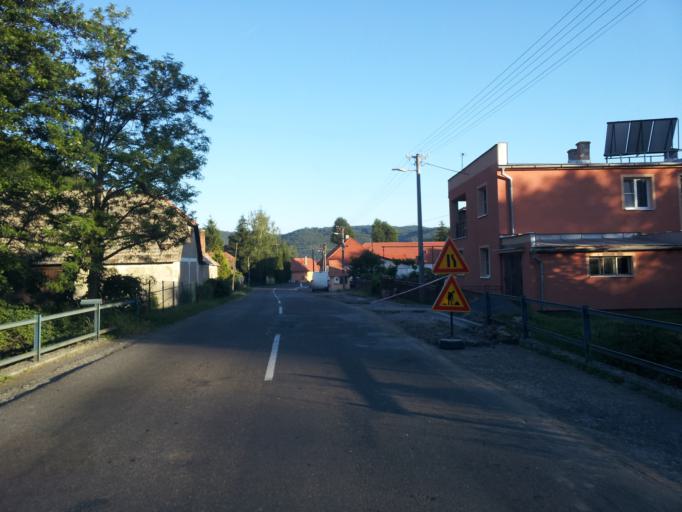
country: SK
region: Banskobystricky
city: Svaety Anton
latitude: 48.3643
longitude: 18.9227
